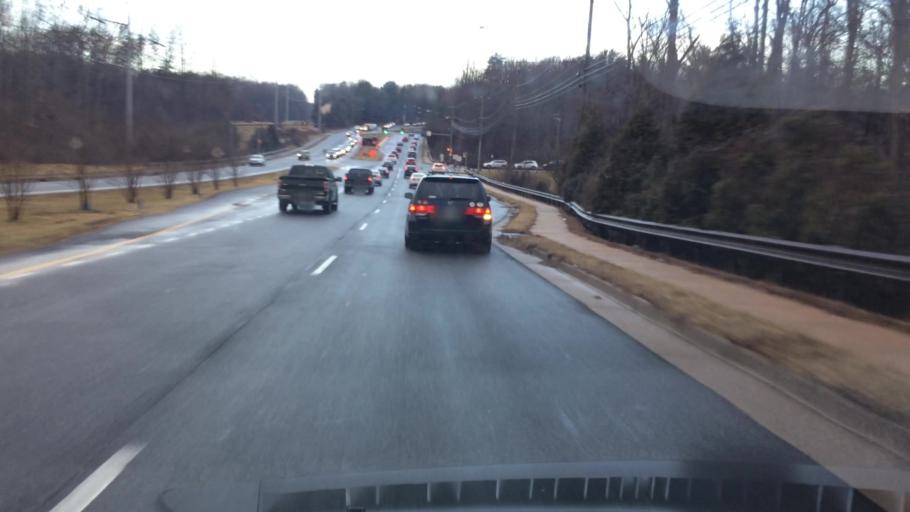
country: US
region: Virginia
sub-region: City of Fairfax
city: Fairfax
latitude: 38.8314
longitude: -77.3302
